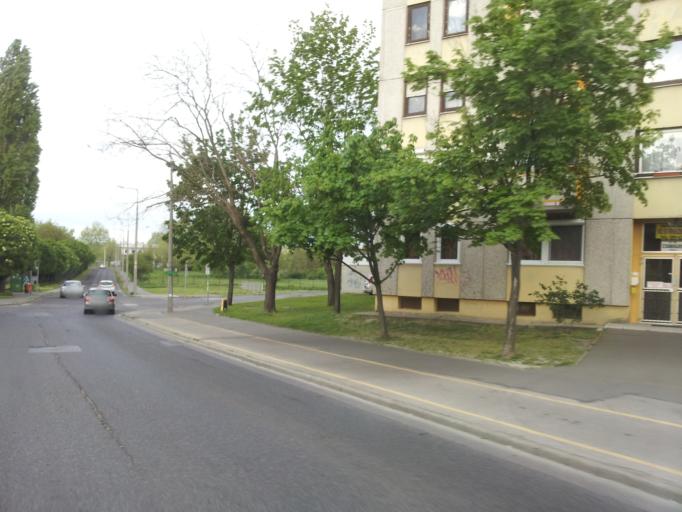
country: HU
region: Budapest
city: Budapest XV. keruelet
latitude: 47.5690
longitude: 19.1265
